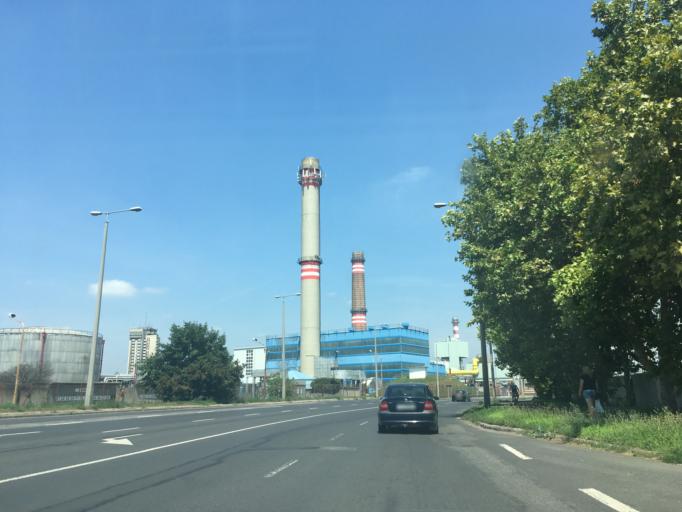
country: HU
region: Hajdu-Bihar
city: Debrecen
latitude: 47.5156
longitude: 21.6294
